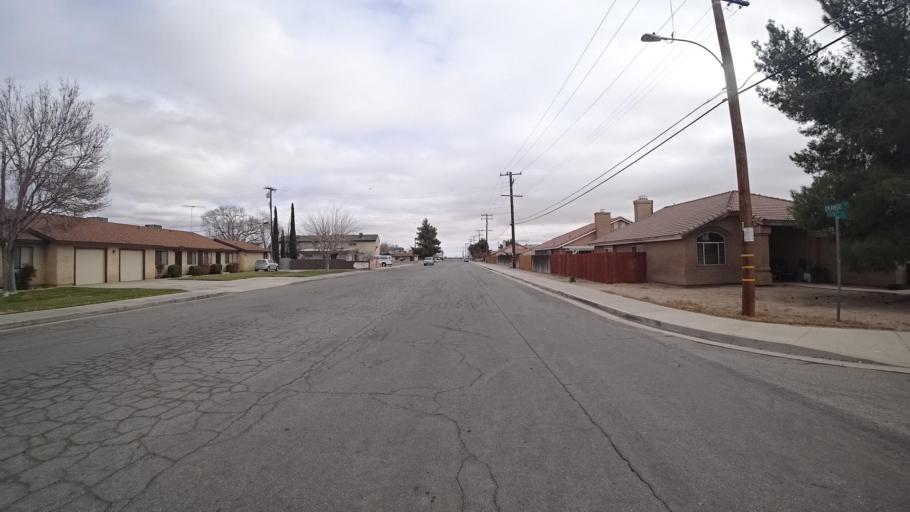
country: US
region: California
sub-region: Kern County
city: Rosamond
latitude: 34.8572
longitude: -118.1661
